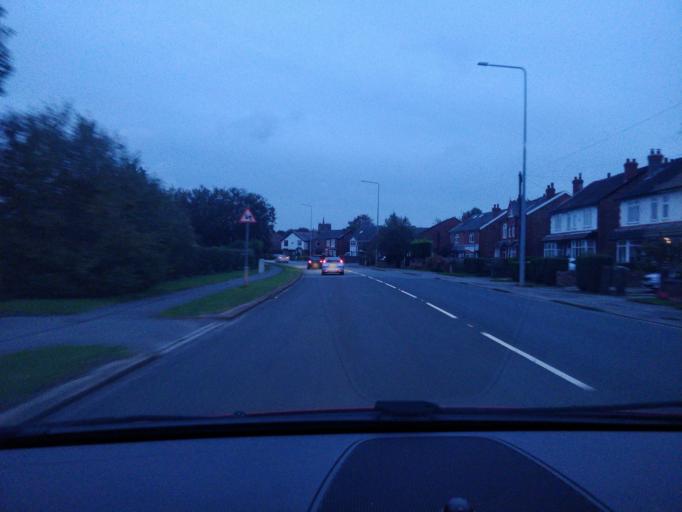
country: GB
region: England
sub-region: Lancashire
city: Ormskirk
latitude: 53.5743
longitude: -2.8935
